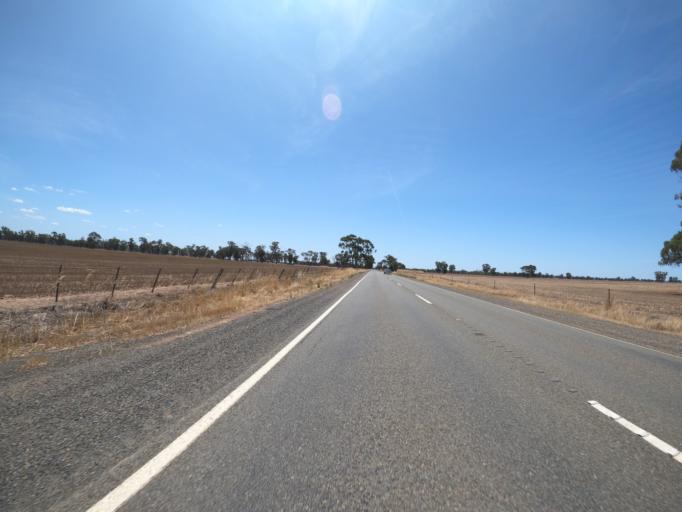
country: AU
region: Victoria
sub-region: Moira
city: Yarrawonga
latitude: -36.1735
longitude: 145.9672
